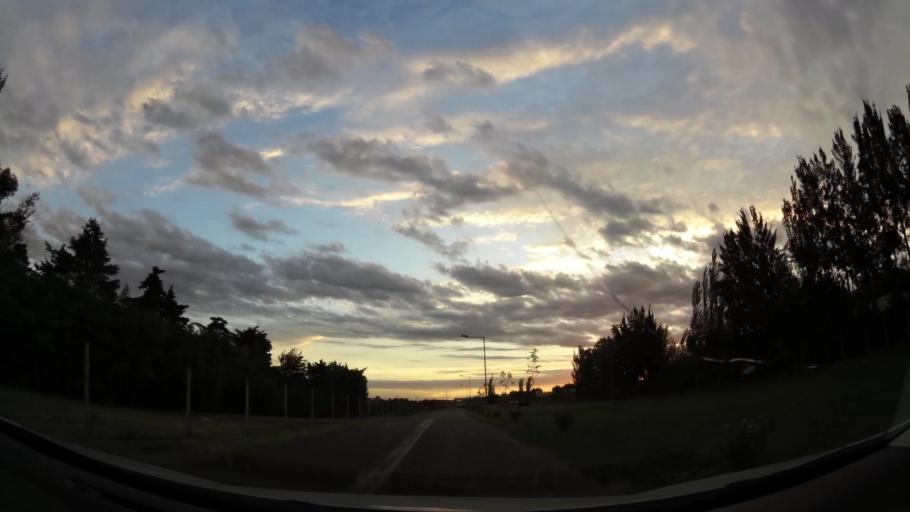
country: AR
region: Buenos Aires
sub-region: Partido de Tigre
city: Tigre
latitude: -34.4437
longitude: -58.6525
